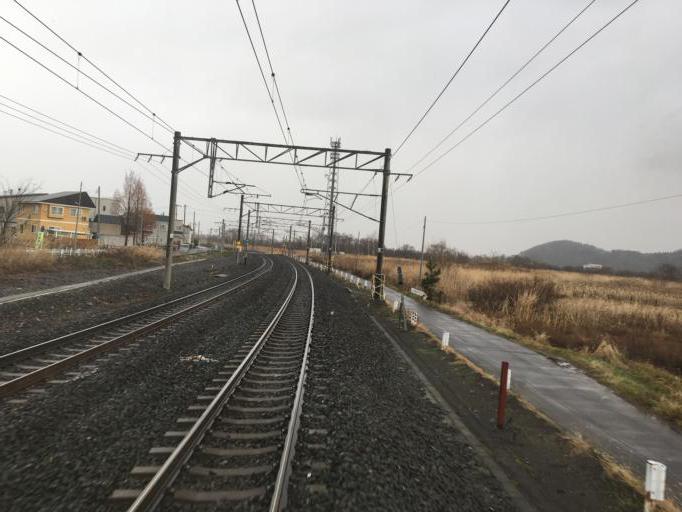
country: JP
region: Aomori
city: Aomori Shi
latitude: 40.8197
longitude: 140.8002
